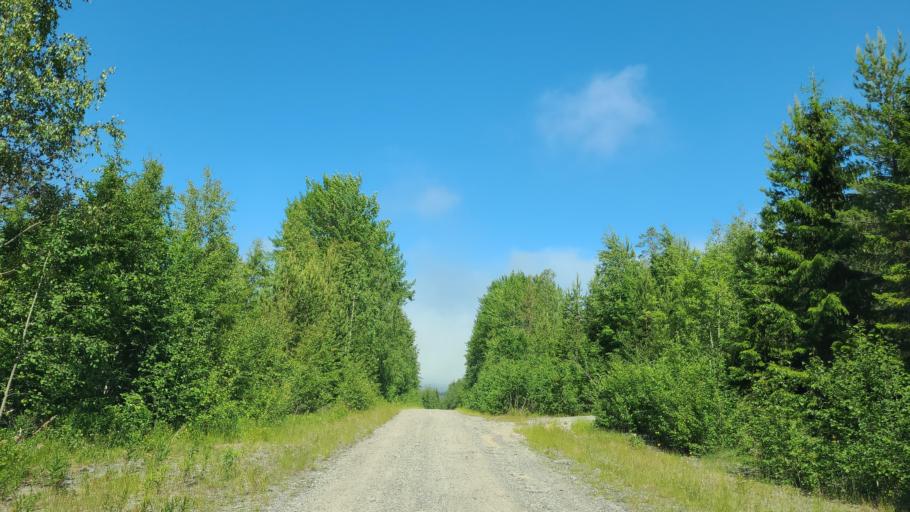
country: SE
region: Vaesternorrland
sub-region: OErnskoeldsviks Kommun
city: Husum
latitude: 63.4471
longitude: 19.2367
